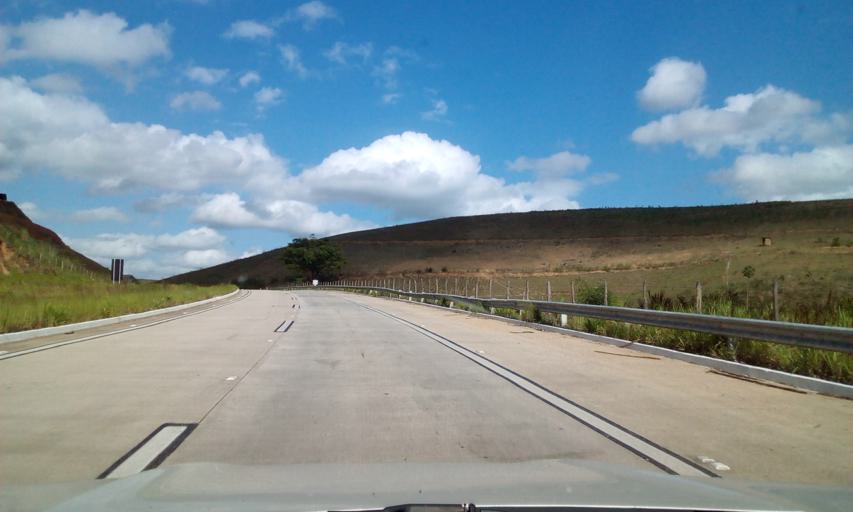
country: BR
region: Alagoas
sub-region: Novo Lino
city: Novo Lino
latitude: -8.9475
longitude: -35.6621
